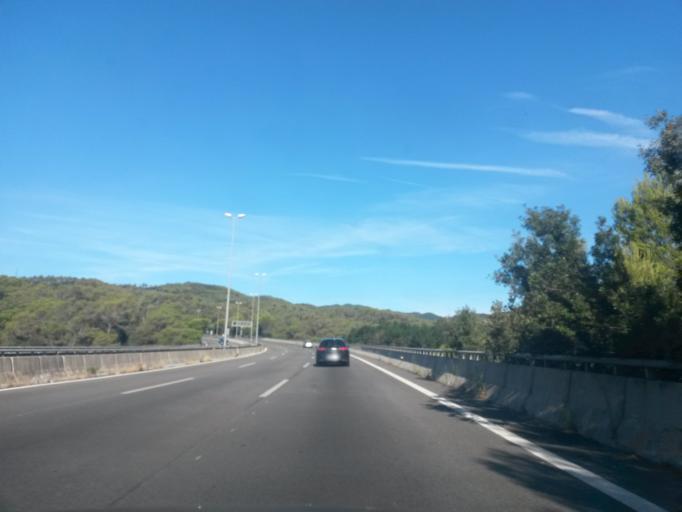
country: ES
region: Catalonia
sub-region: Provincia de Barcelona
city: Pineda de Mar
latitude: 41.6521
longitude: 2.6930
